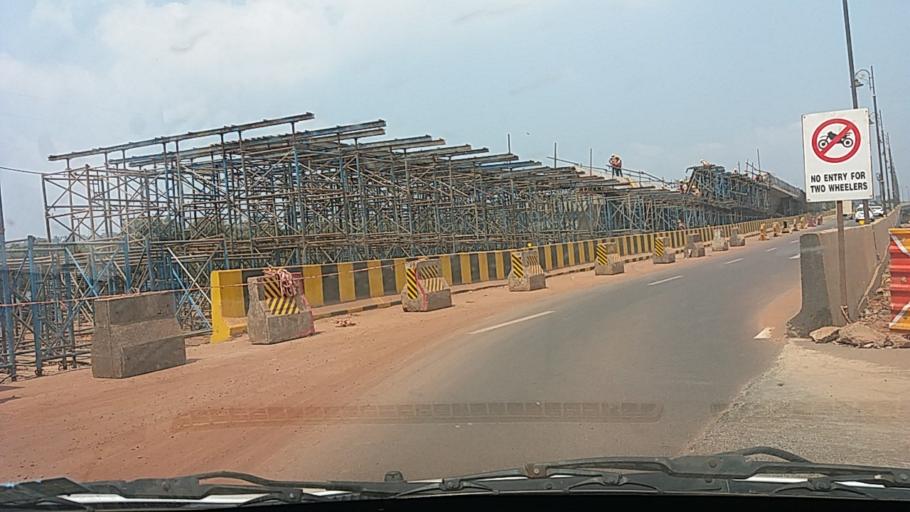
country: IN
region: Goa
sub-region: North Goa
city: Panaji
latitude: 15.4925
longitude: 73.8420
